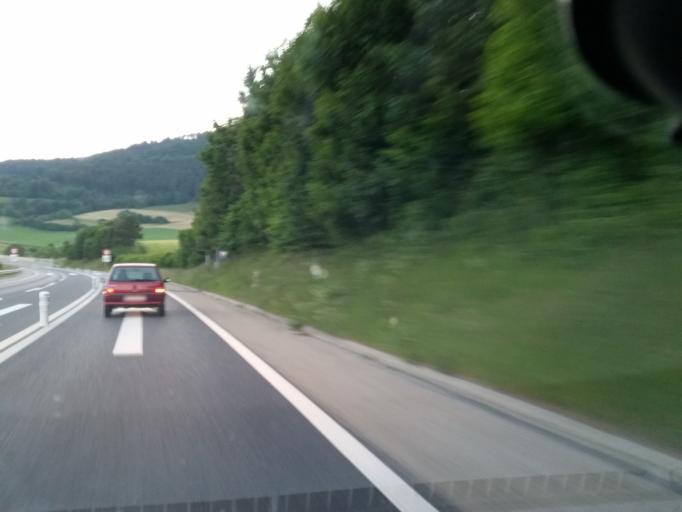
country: CH
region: Vaud
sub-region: Jura-Nord vaudois District
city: Orbe
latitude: 46.7378
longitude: 6.4613
